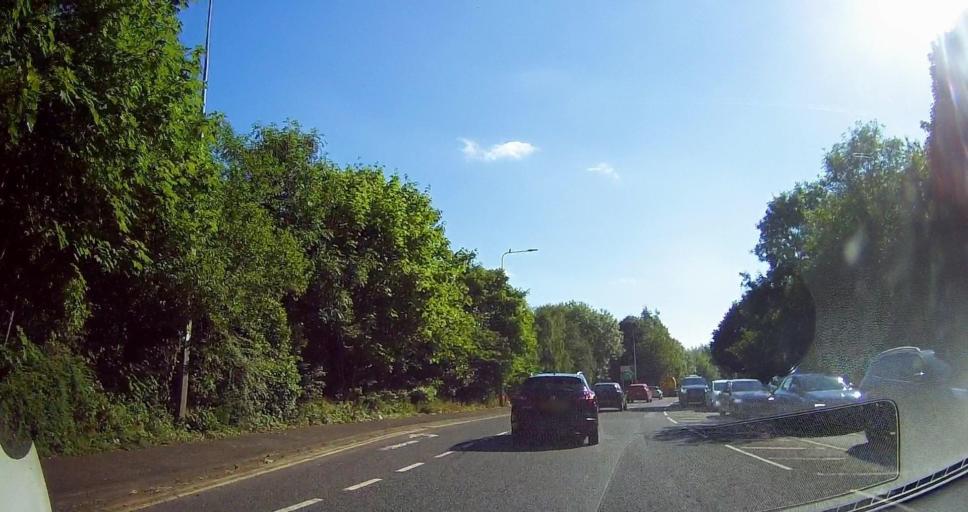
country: GB
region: England
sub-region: Cheshire East
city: Sandbach
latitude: 53.1424
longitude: -2.3585
